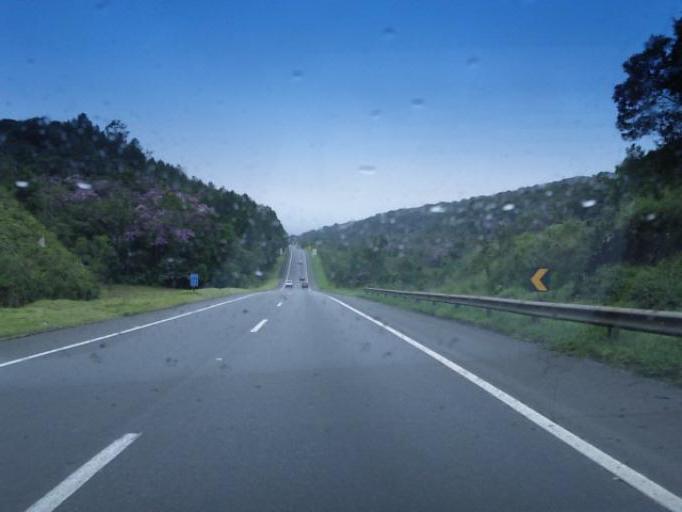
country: BR
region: Sao Paulo
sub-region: Cajati
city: Cajati
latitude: -24.9687
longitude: -48.4431
